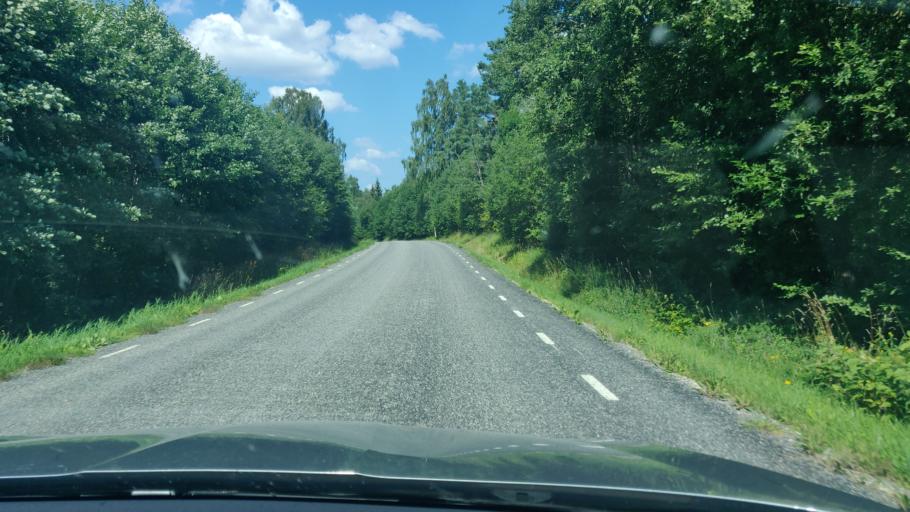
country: EE
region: Tartu
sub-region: Elva linn
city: Elva
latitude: 58.1503
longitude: 26.4734
